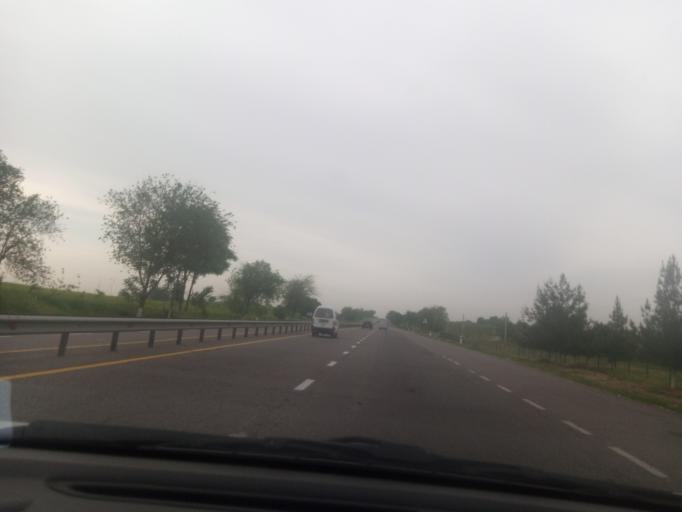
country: UZ
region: Toshkent
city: Tuytepa
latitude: 41.1158
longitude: 69.4451
